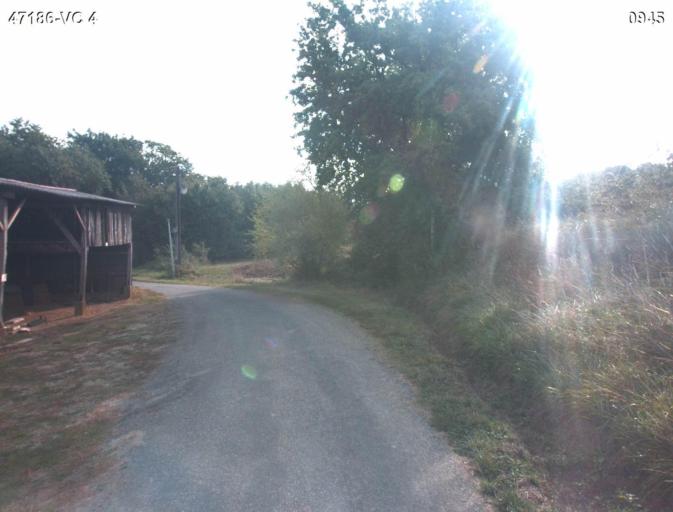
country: FR
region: Aquitaine
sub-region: Departement du Lot-et-Garonne
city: Port-Sainte-Marie
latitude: 44.2014
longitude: 0.4276
